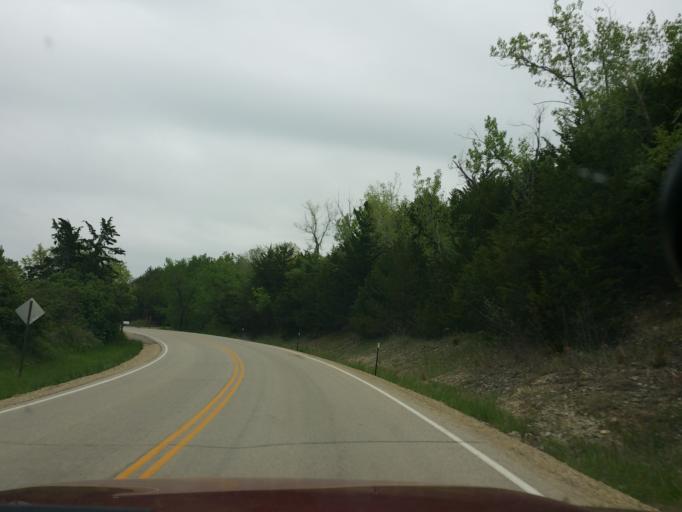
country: US
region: Kansas
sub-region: Riley County
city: Manhattan
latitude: 39.2680
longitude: -96.6257
